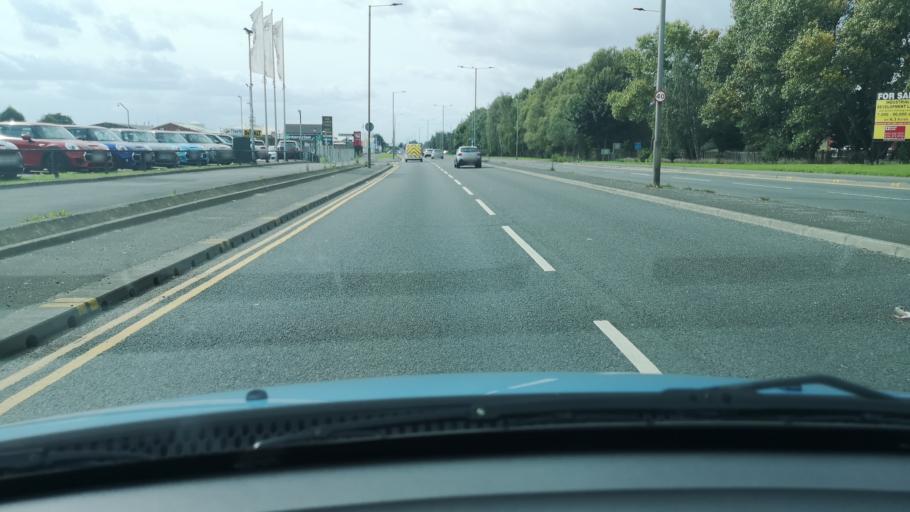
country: GB
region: England
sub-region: Doncaster
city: Kirk Sandall
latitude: 53.5474
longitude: -1.0918
